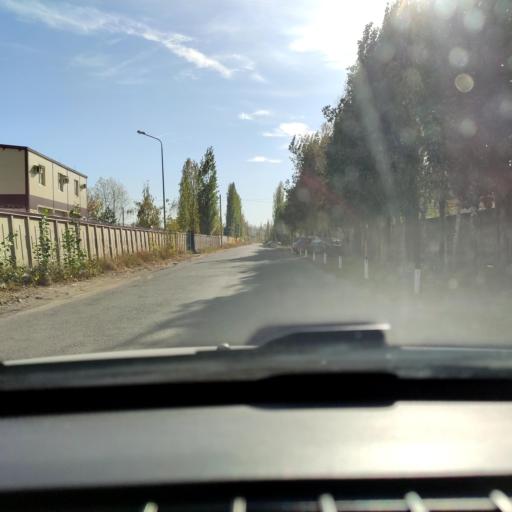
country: RU
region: Voronezj
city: Podgornoye
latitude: 51.8070
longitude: 39.2003
